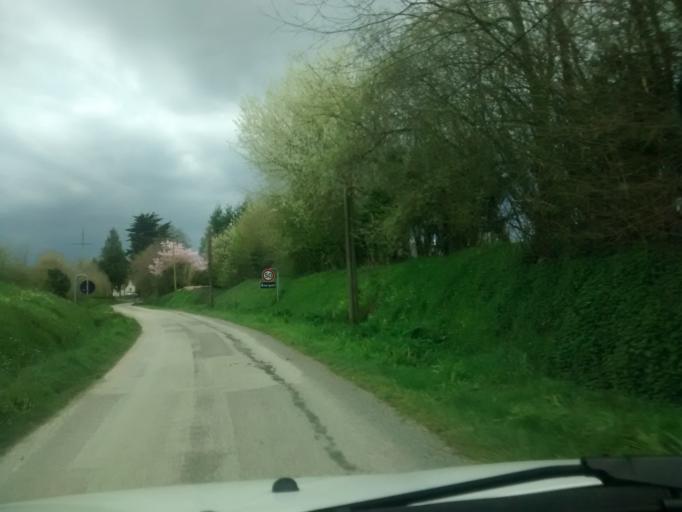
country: FR
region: Brittany
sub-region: Departement d'Ille-et-Vilaine
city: Brece
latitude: 48.1438
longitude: -1.4948
